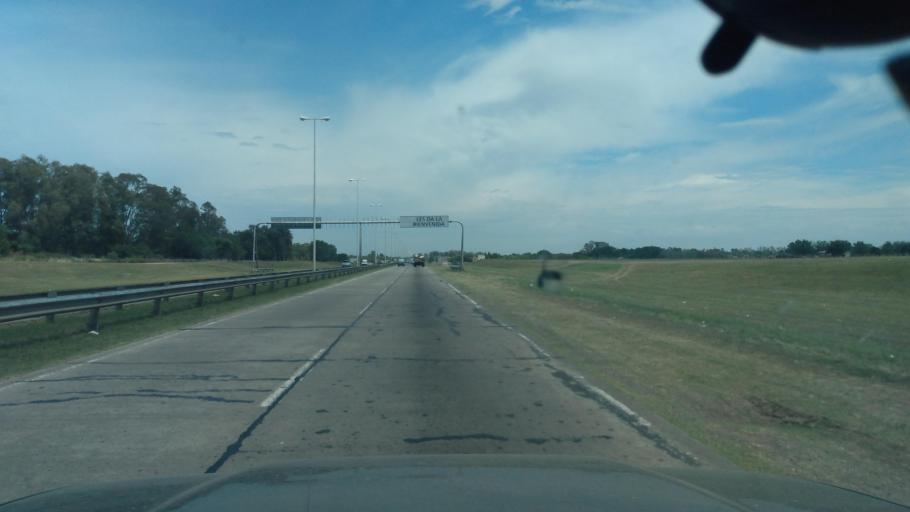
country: AR
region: Buenos Aires
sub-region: Partido de Lujan
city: Lujan
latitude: -34.5664
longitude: -59.0706
